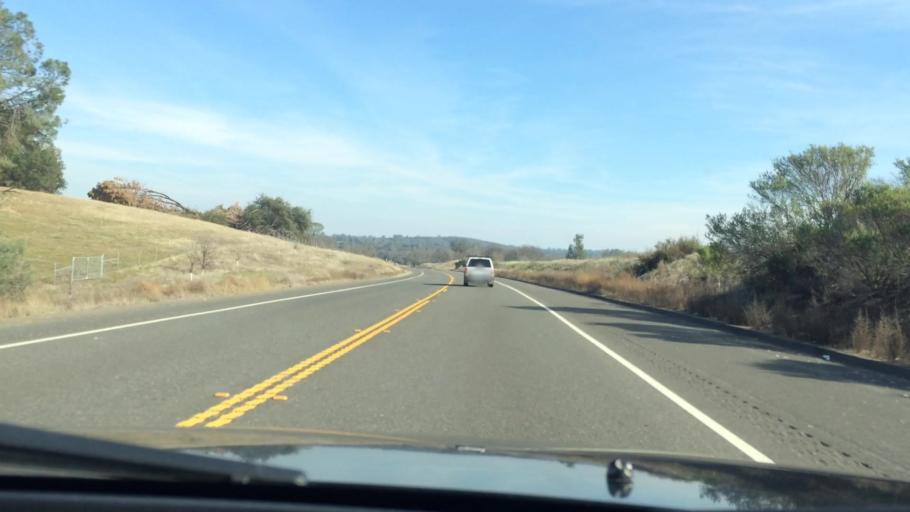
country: US
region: California
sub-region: Sacramento County
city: Rancho Murieta
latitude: 38.4809
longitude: -121.0366
